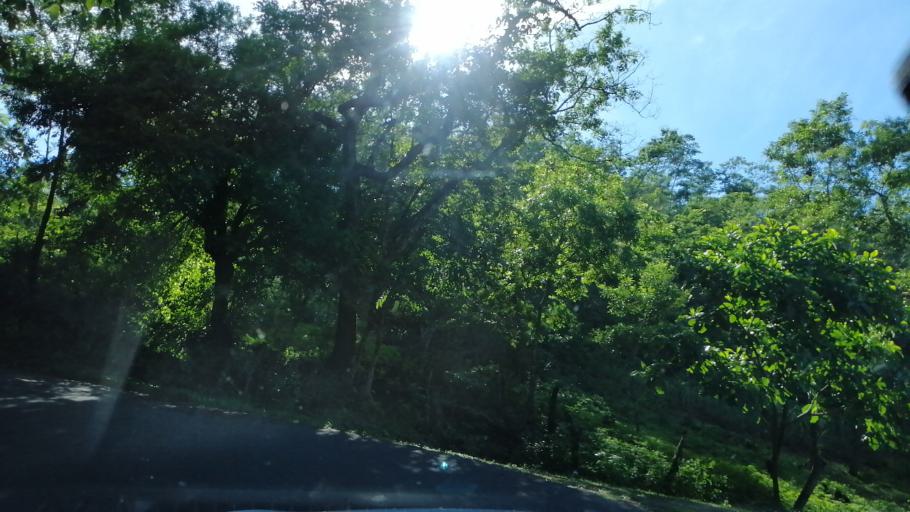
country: SV
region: Morazan
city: Cacaopera
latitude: 13.7859
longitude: -88.0326
